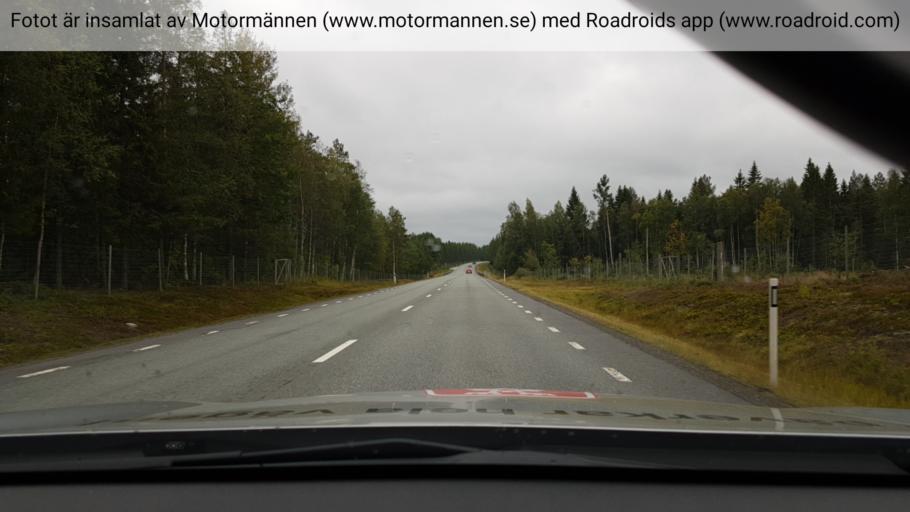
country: SE
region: Vaesterbotten
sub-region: Robertsfors Kommun
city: Robertsfors
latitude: 64.0502
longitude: 20.8485
